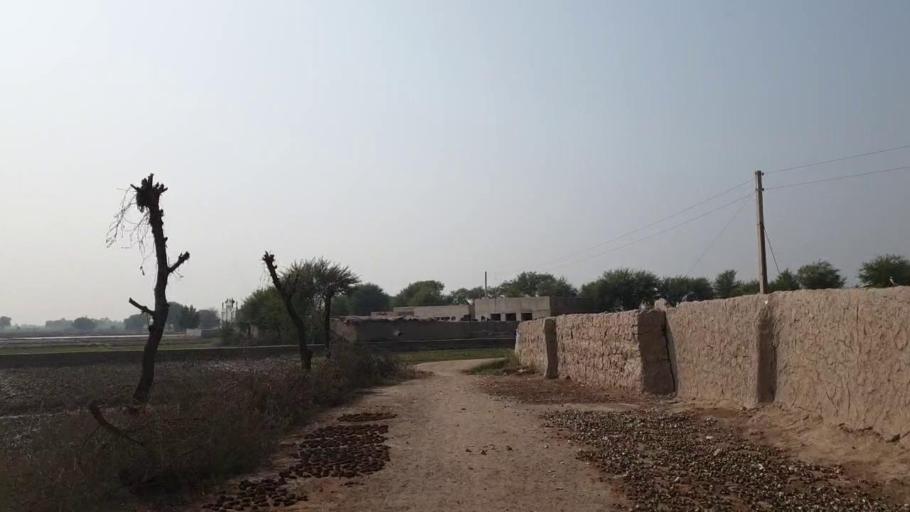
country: PK
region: Sindh
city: Bhan
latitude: 26.4617
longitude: 67.7376
